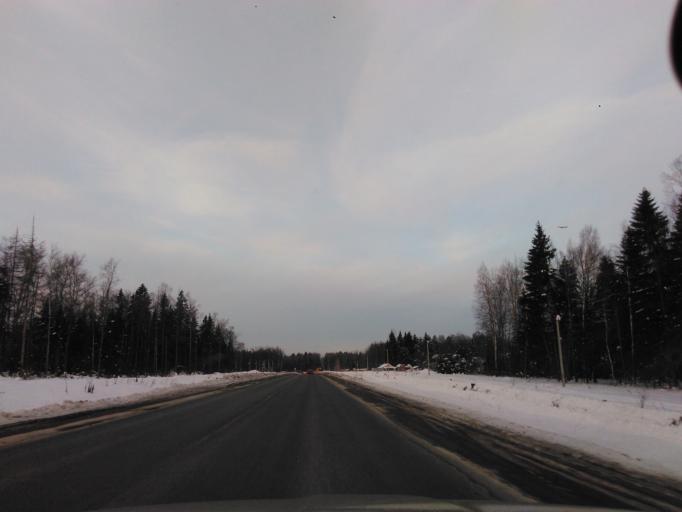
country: RU
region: Moskovskaya
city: Povarovo
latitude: 56.0231
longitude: 37.0432
